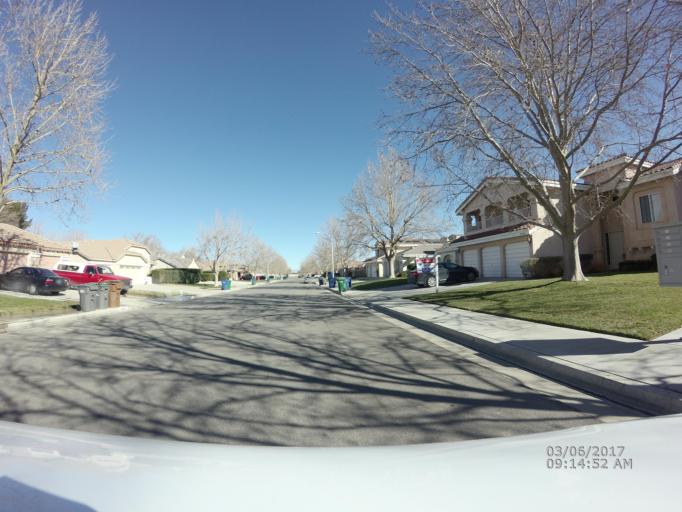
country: US
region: California
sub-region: Los Angeles County
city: Quartz Hill
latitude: 34.6538
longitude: -118.2116
